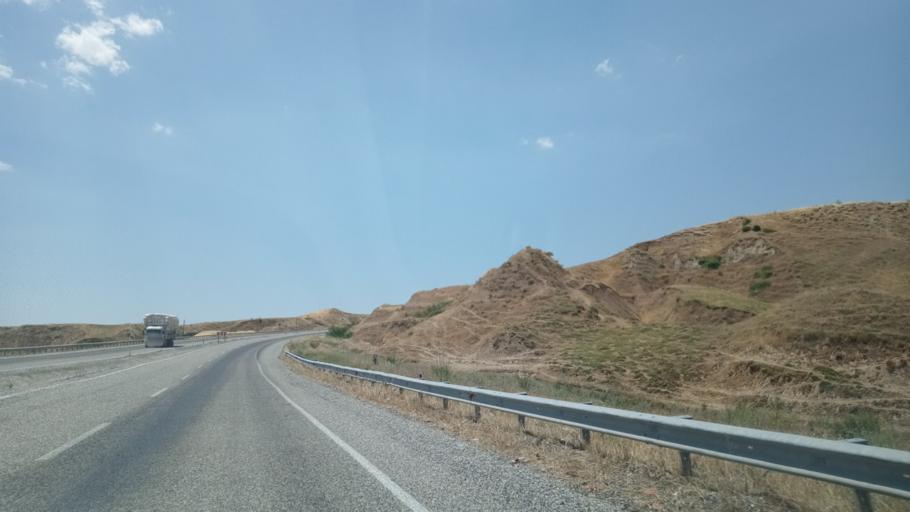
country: TR
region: Batman
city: Bekirhan
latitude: 38.1382
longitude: 41.2749
